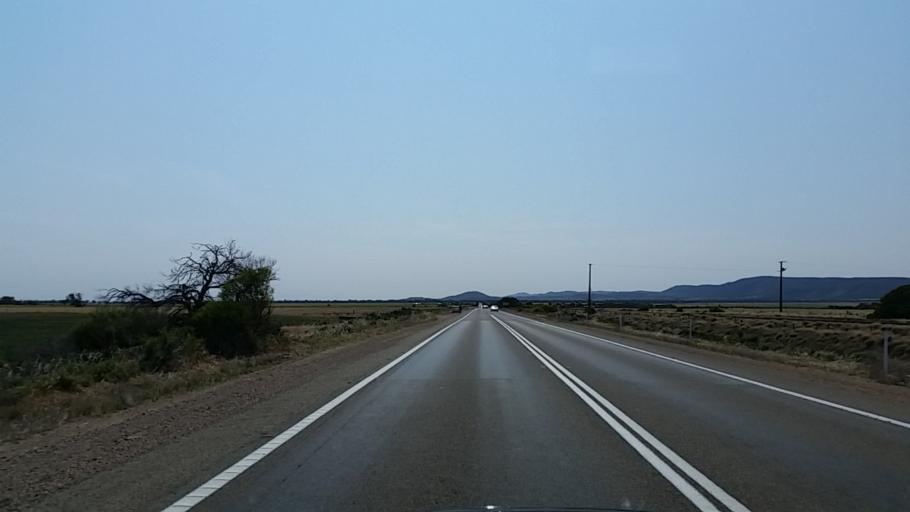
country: AU
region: South Australia
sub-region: Port Pirie City and Dists
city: Port Pirie
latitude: -32.9014
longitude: 137.9823
